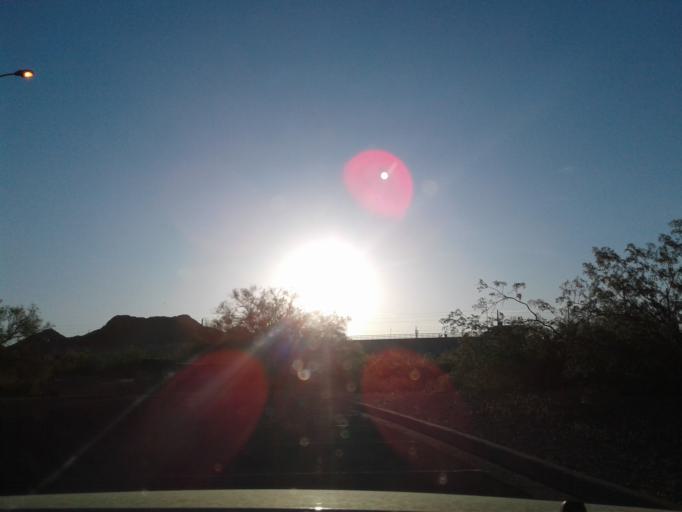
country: US
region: Arizona
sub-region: Maricopa County
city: Phoenix
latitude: 33.5318
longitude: -112.0361
